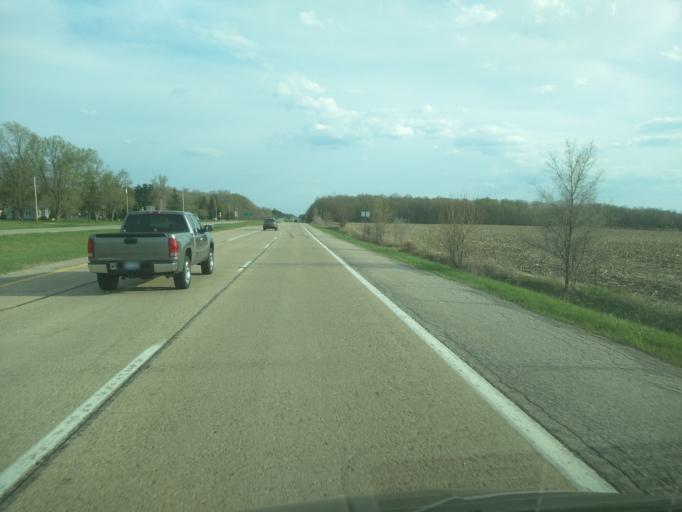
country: US
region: Michigan
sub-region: Eaton County
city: Dimondale
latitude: 42.6381
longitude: -84.6233
